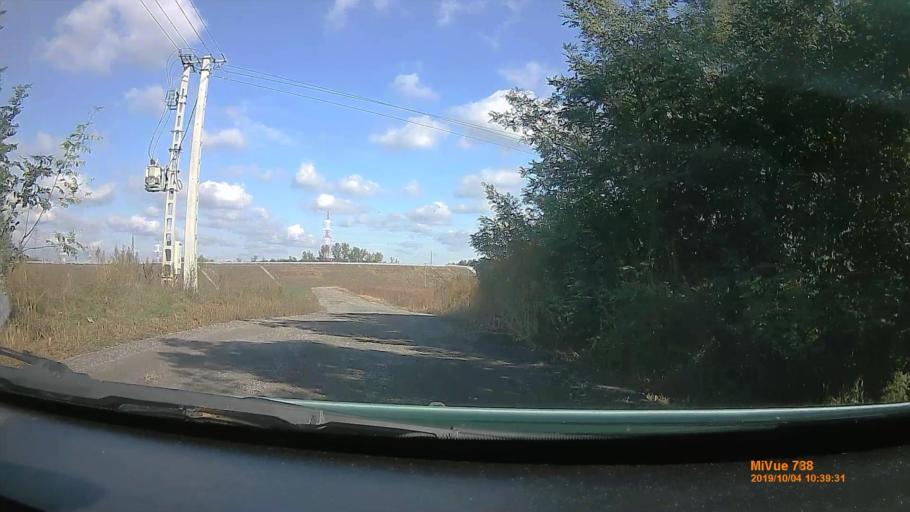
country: HU
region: Szabolcs-Szatmar-Bereg
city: Nyirtelek
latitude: 47.9759
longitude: 21.6636
